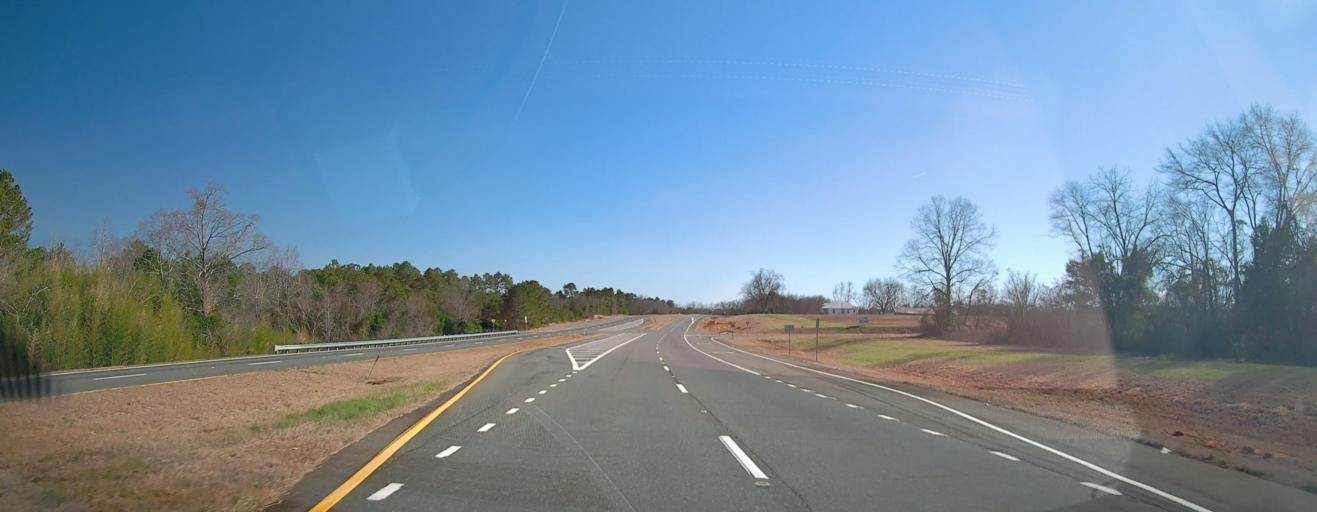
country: US
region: Georgia
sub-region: Sumter County
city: Americus
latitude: 32.1249
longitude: -84.2646
